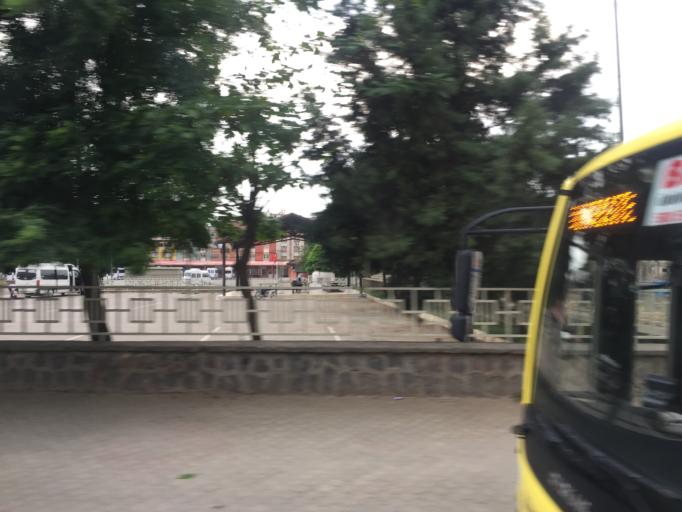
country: TR
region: Gaziantep
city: Gaziantep
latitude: 37.0684
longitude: 37.4140
